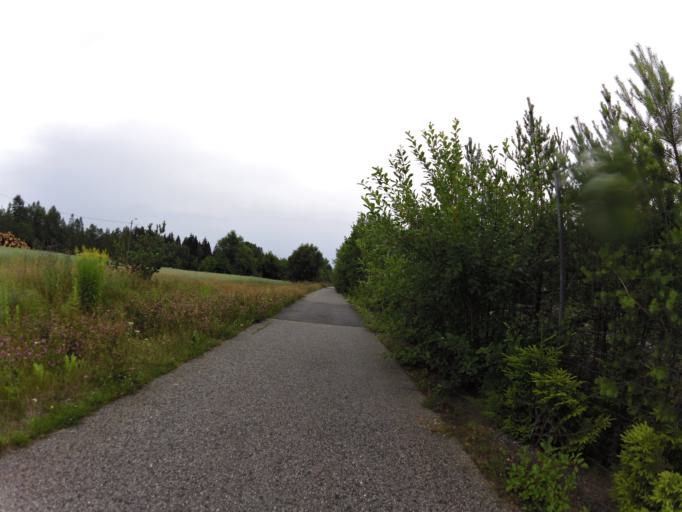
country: NO
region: Ostfold
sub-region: Moss
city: Moss
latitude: 59.5096
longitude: 10.7217
